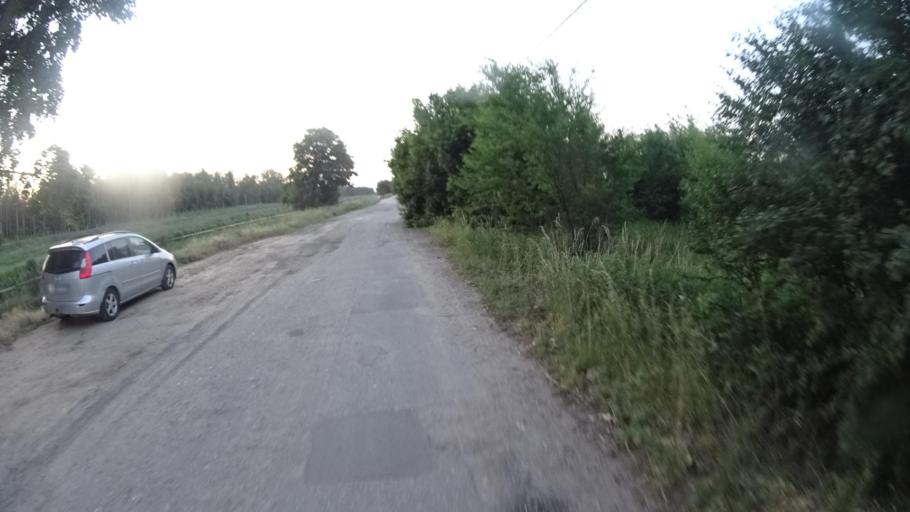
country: PL
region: Masovian Voivodeship
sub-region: Powiat legionowski
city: Stanislawow Pierwszy
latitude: 52.3412
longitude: 21.0336
